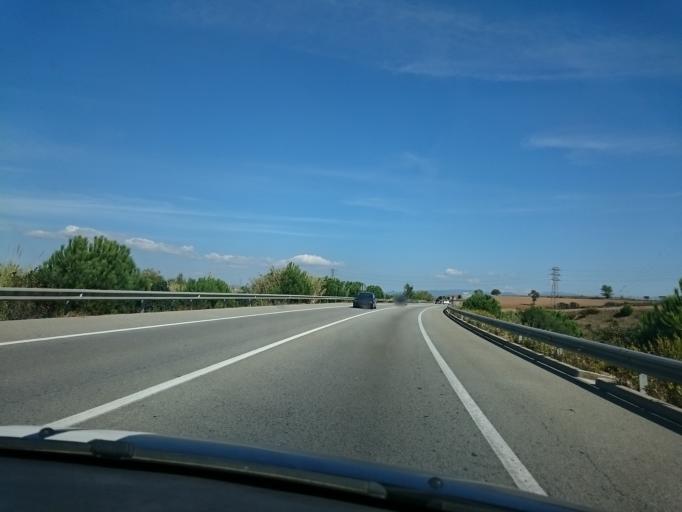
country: ES
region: Catalonia
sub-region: Provincia de Barcelona
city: Santa Perpetua de Mogoda
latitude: 41.5586
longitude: 2.1857
